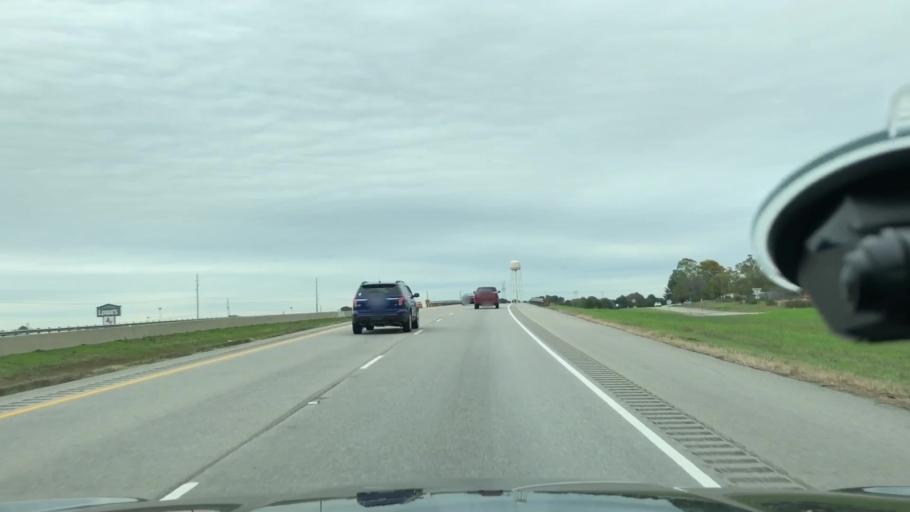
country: US
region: Texas
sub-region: Franklin County
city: Mount Vernon
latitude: 33.1621
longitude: -95.1780
